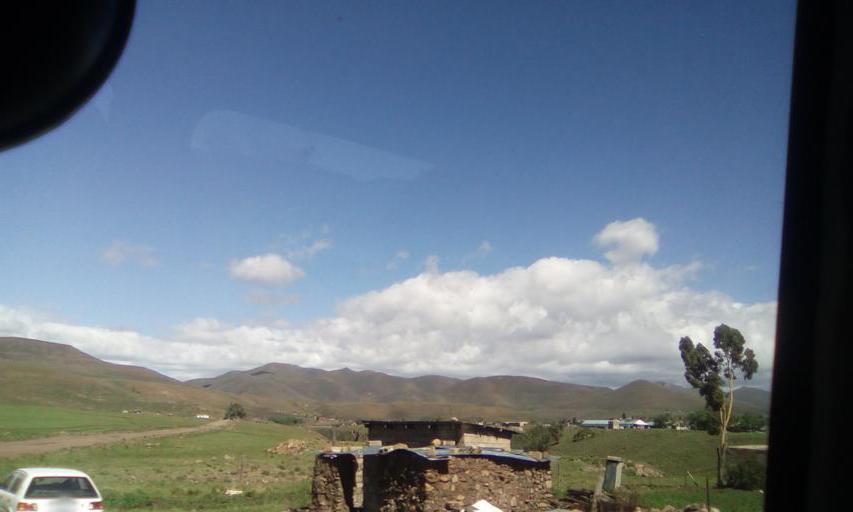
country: LS
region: Maseru
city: Nako
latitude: -29.8468
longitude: 28.0574
